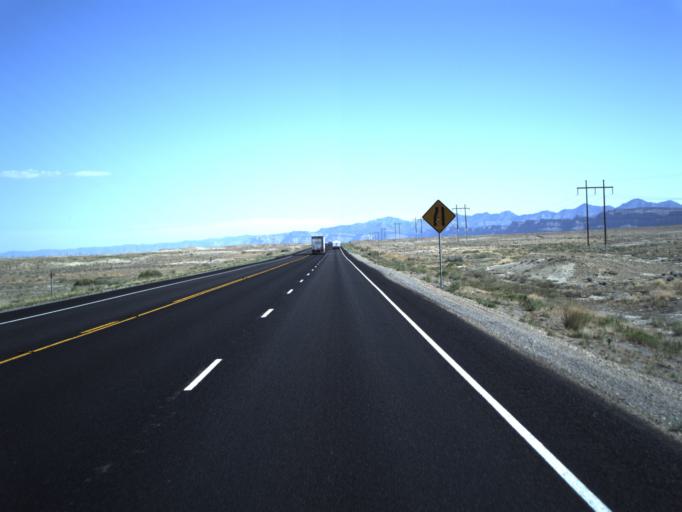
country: US
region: Utah
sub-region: Carbon County
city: East Carbon City
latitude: 39.1728
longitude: -110.3383
